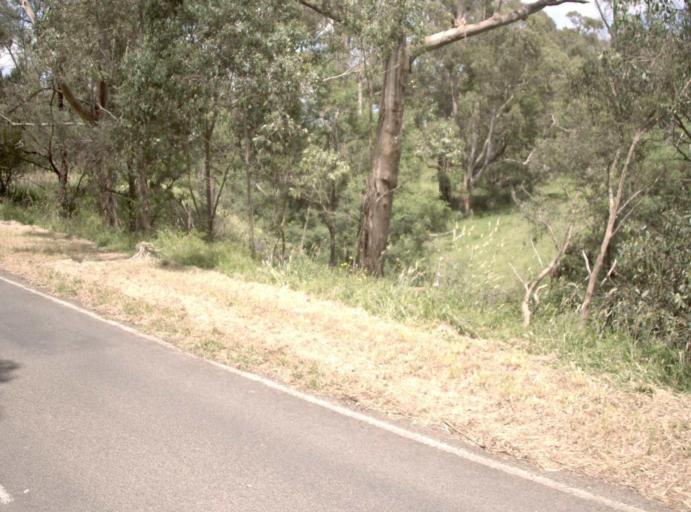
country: AU
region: Victoria
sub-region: Baw Baw
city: Warragul
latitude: -38.5083
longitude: 146.0052
